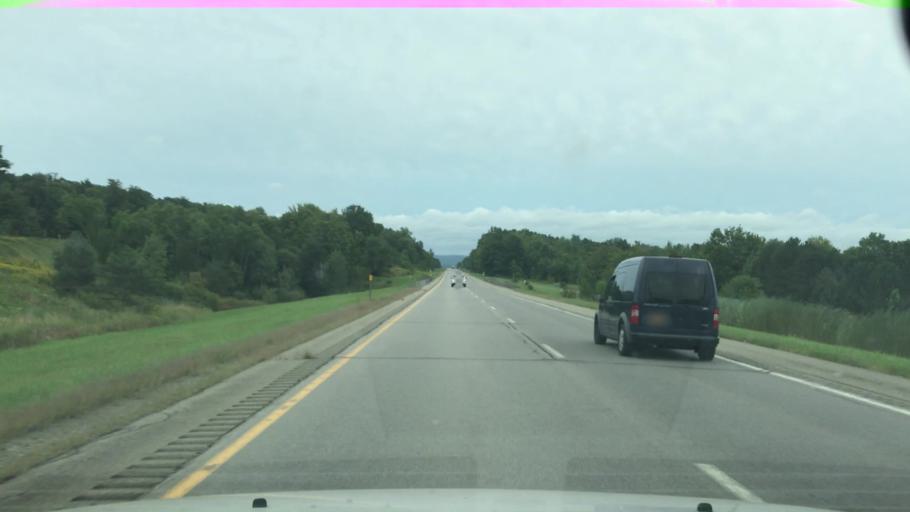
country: US
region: New York
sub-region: Erie County
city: Springville
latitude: 42.5375
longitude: -78.7078
